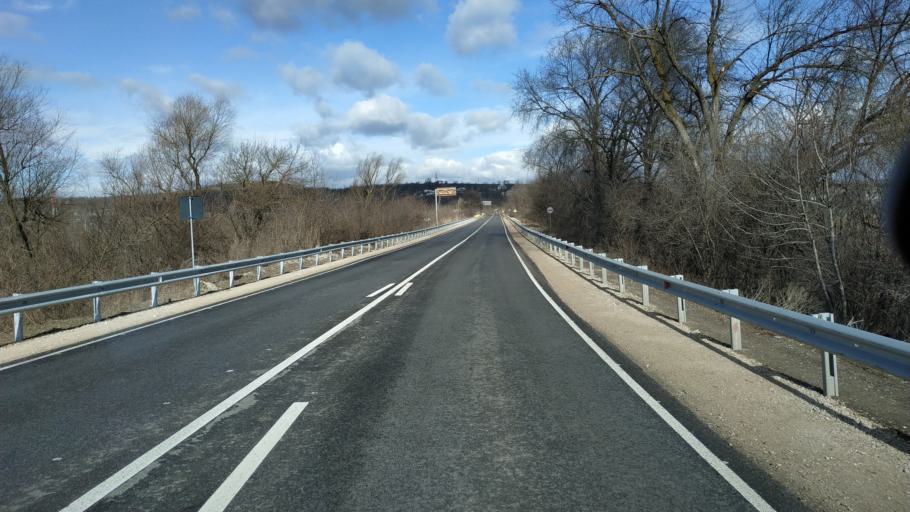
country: MD
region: Stinga Nistrului
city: Bucovat
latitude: 47.1815
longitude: 28.4673
